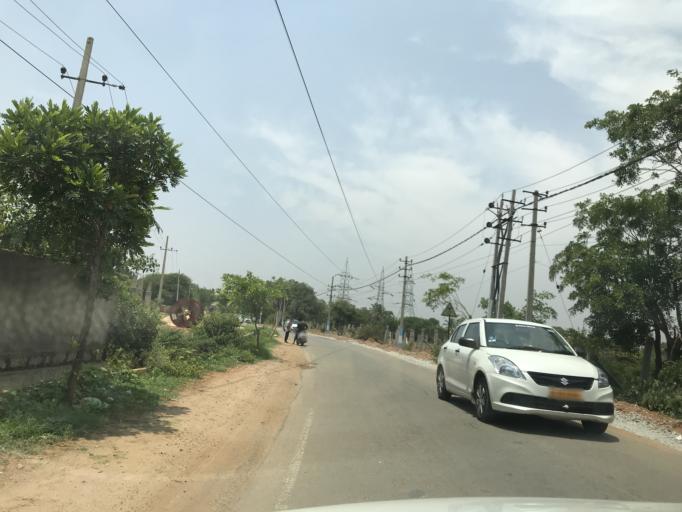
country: IN
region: Karnataka
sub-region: Bangalore Rural
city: Devanhalli
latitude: 13.1811
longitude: 77.6679
